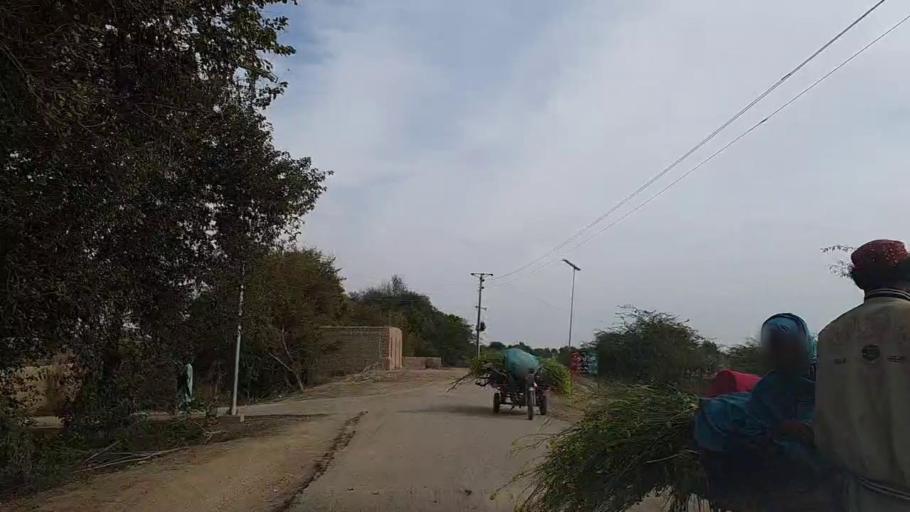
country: PK
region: Sindh
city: Jam Sahib
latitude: 26.4390
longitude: 68.6257
